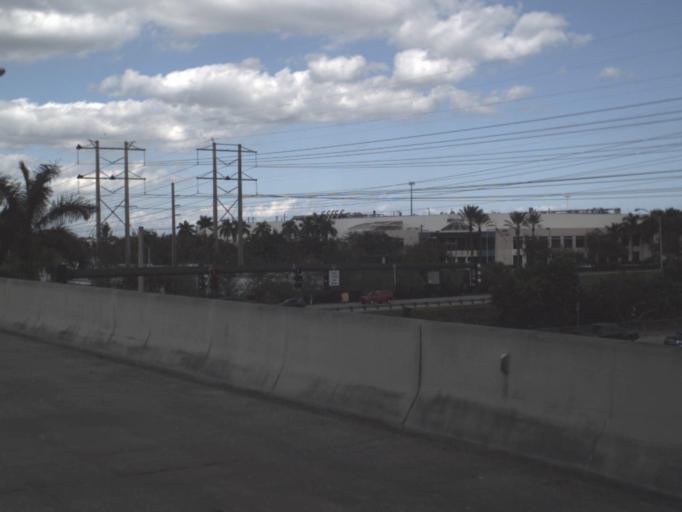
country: US
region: Florida
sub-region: Broward County
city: Davie
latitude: 26.0652
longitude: -80.2153
